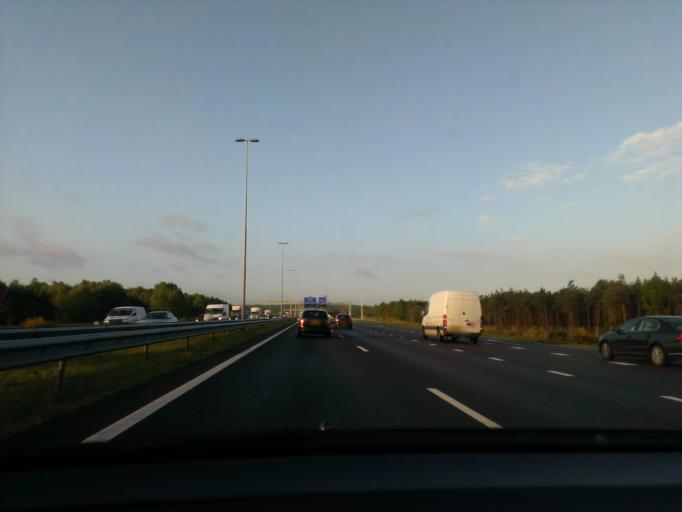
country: NL
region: Gelderland
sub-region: Gemeente Rozendaal
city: Rozendaal
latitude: 52.0304
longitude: 5.9271
